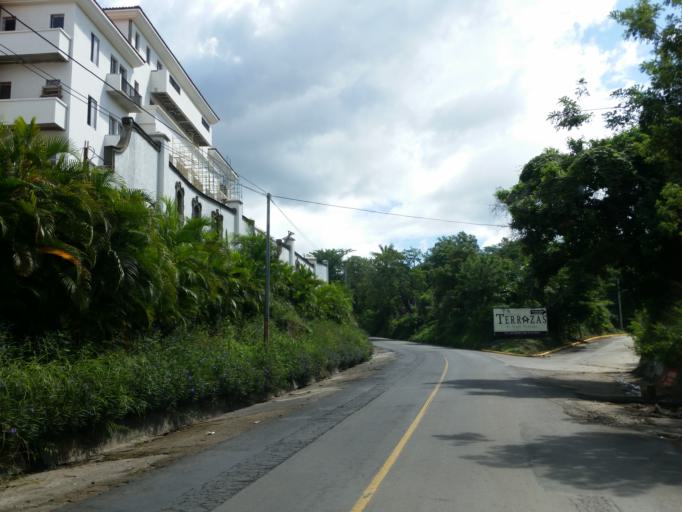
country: NI
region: Managua
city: Managua
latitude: 12.0959
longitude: -86.2482
